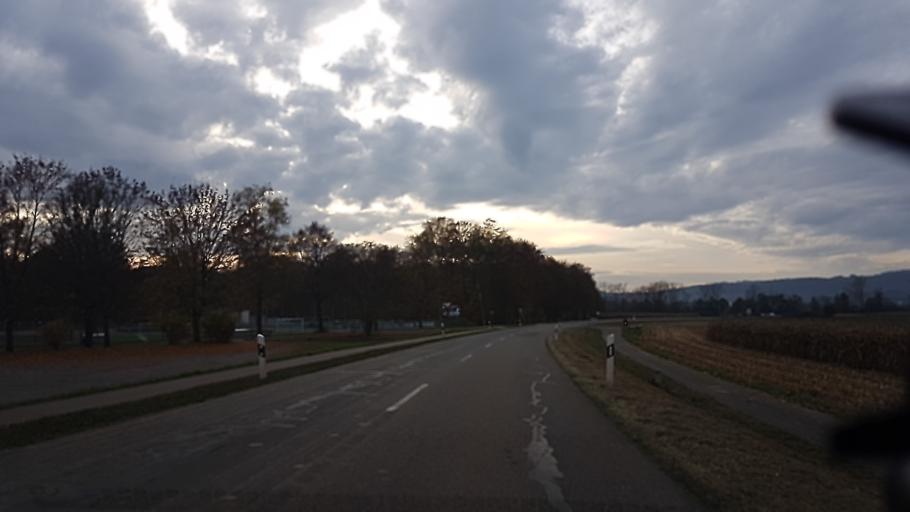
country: DE
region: Baden-Wuerttemberg
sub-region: Freiburg Region
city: Eichstetten
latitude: 48.0692
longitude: 7.7553
